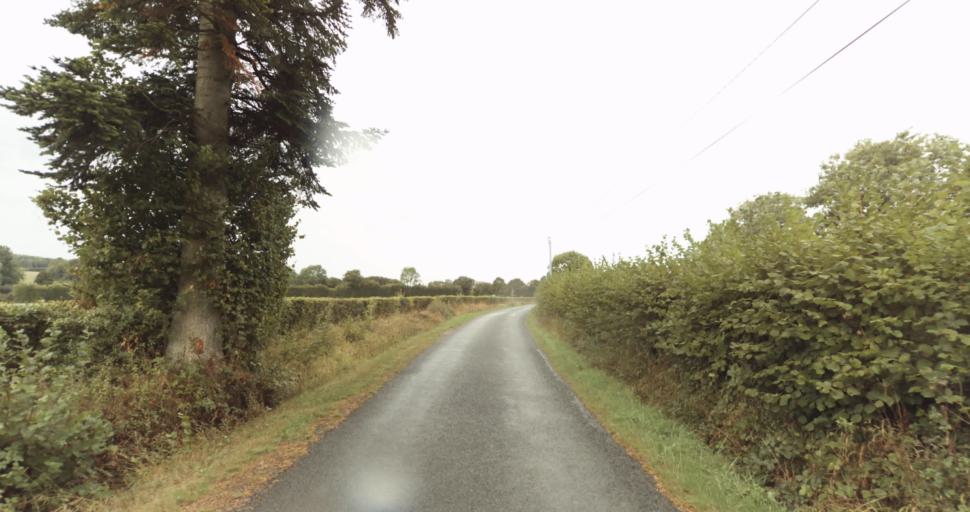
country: FR
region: Lower Normandy
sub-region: Departement de l'Orne
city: Sainte-Gauburge-Sainte-Colombe
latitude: 48.6891
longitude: 0.4204
